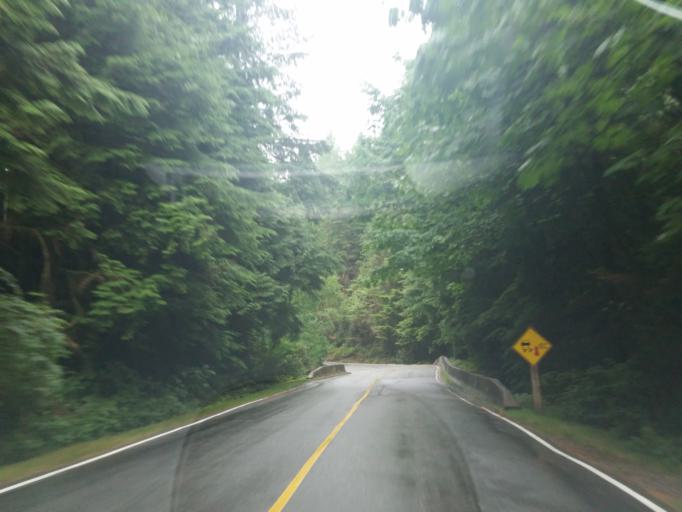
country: CA
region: British Columbia
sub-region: Greater Vancouver Regional District
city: Anmore
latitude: 49.3145
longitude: -122.8911
